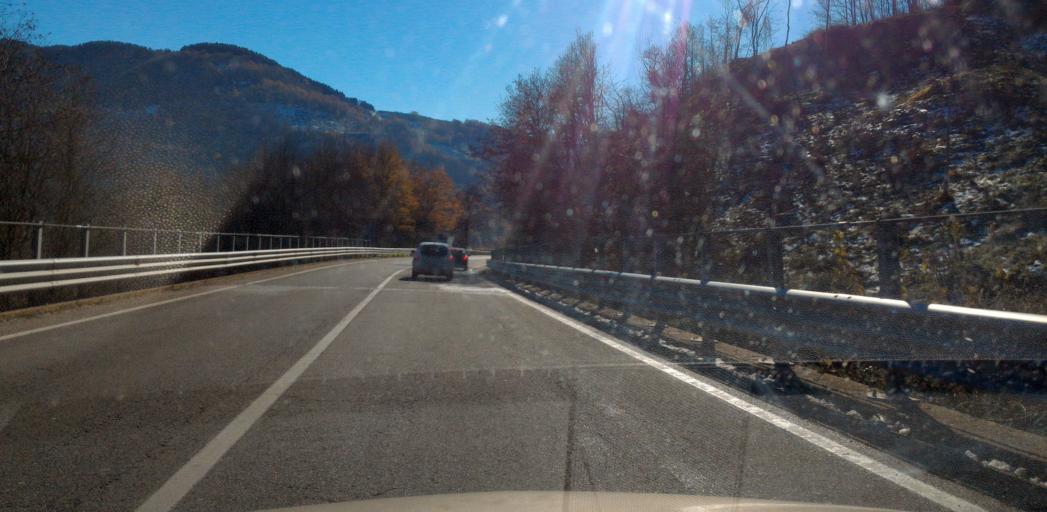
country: IT
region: Calabria
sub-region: Provincia di Cosenza
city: Spezzano della Sila
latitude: 39.3027
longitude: 16.3549
